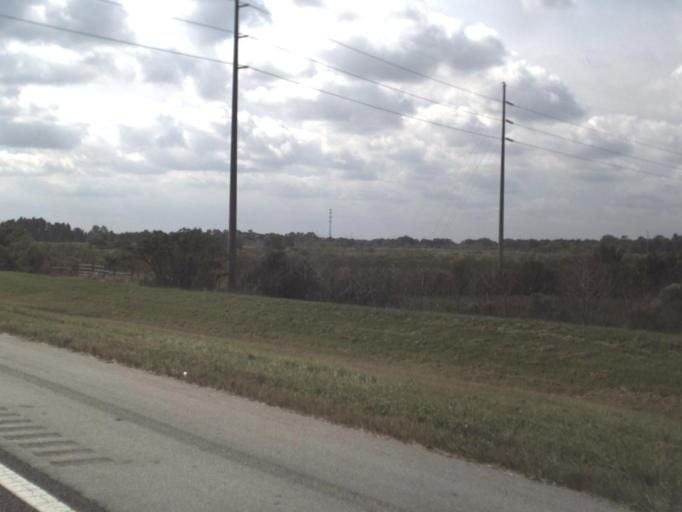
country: US
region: Florida
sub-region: Polk County
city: Fussels Corner
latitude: 28.0603
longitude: -81.8347
